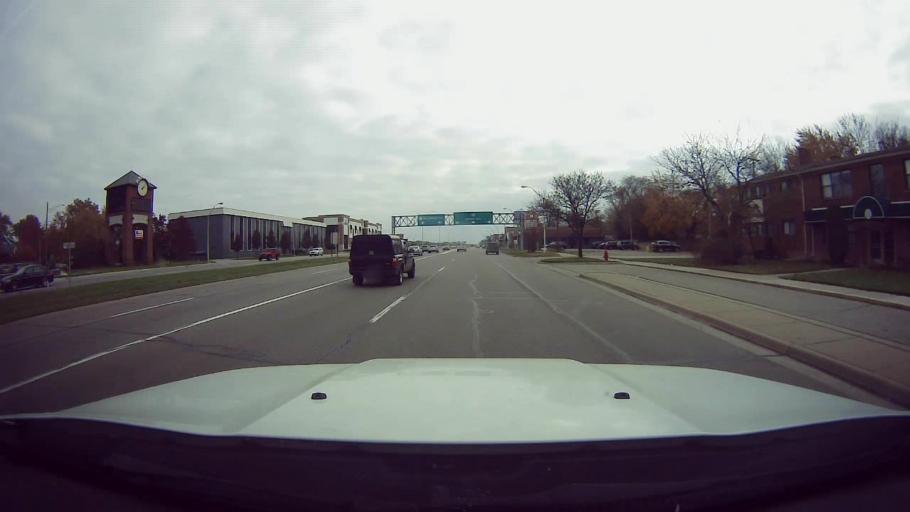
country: US
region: Michigan
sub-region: Oakland County
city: Royal Oak
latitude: 42.4808
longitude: -83.1509
